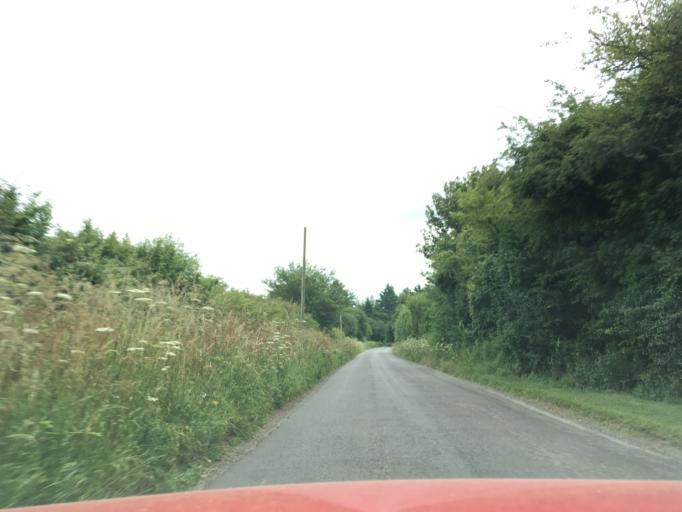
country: GB
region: England
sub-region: Oxfordshire
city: Chipping Norton
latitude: 51.9235
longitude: -1.5476
